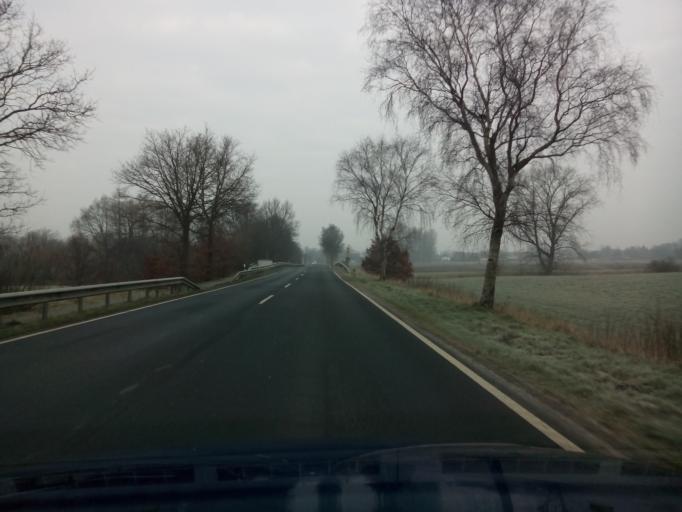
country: DE
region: Lower Saxony
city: Loxstedt
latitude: 53.4497
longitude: 8.6119
